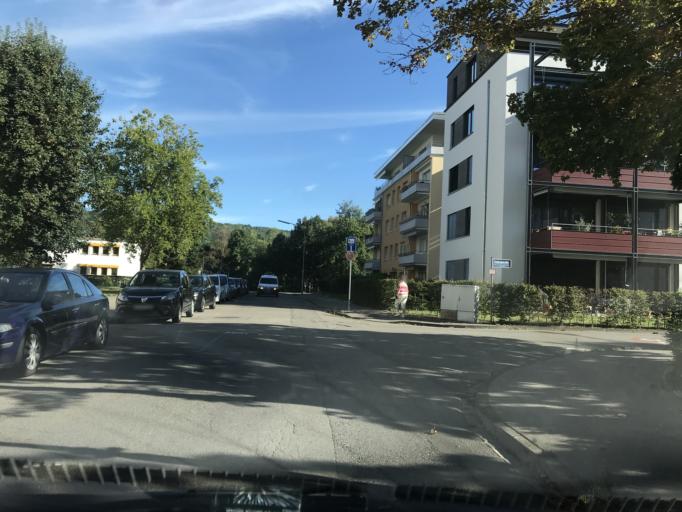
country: DE
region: Baden-Wuerttemberg
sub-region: Freiburg Region
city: Loerrach
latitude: 47.6243
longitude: 7.6675
